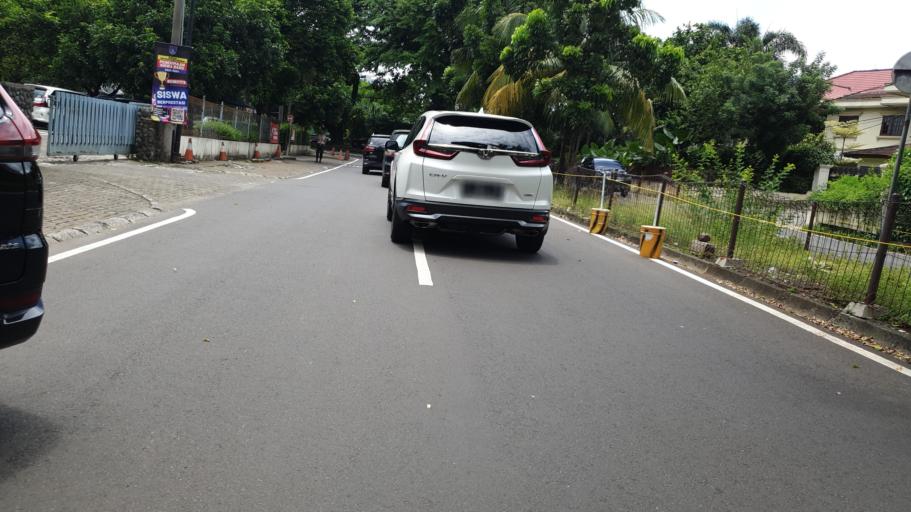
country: ID
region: Banten
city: South Tangerang
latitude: -6.2837
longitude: 106.7878
